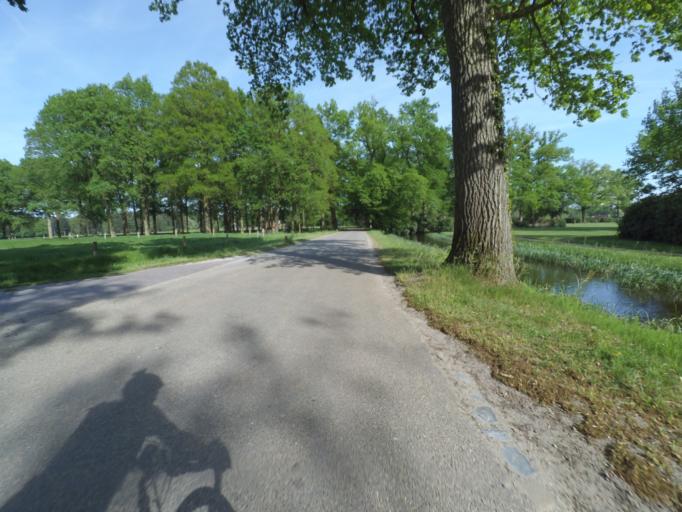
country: NL
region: Overijssel
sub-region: Gemeente Oldenzaal
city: Oldenzaal
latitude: 52.3761
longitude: 6.9817
